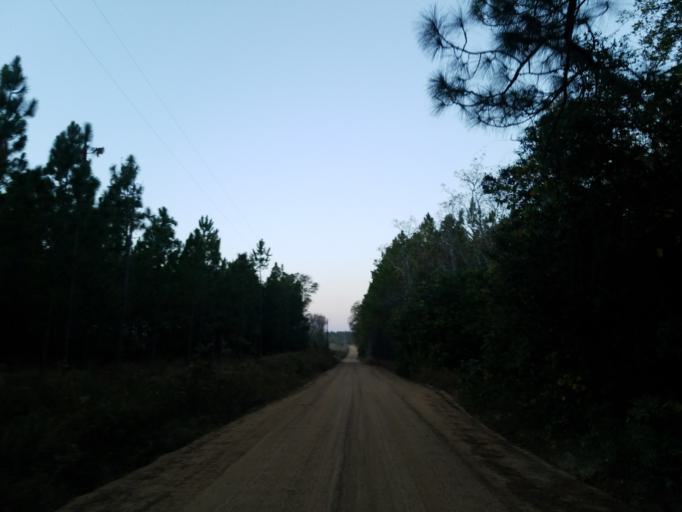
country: US
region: Georgia
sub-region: Turner County
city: Ashburn
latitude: 31.7395
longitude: -83.4848
